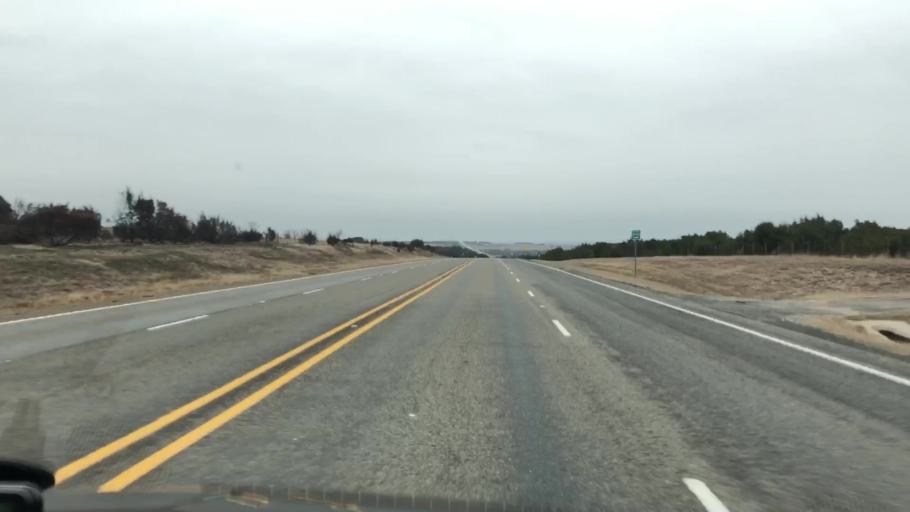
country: US
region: Texas
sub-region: Lampasas County
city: Lampasas
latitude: 31.1934
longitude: -98.1719
